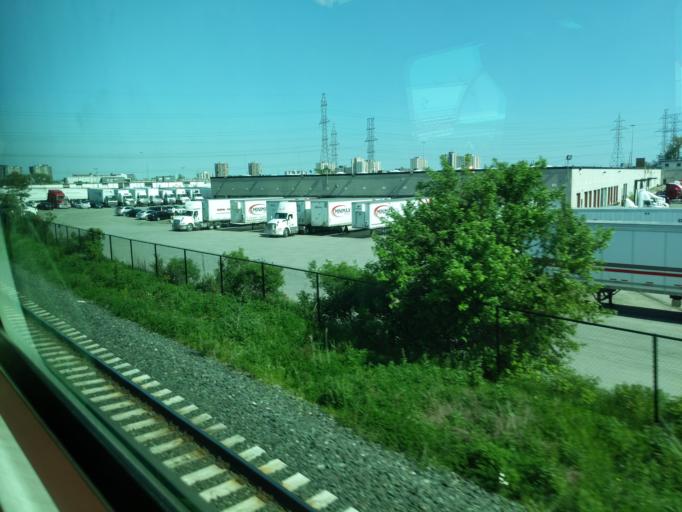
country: CA
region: Ontario
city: Etobicoke
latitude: 43.7062
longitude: -79.5692
